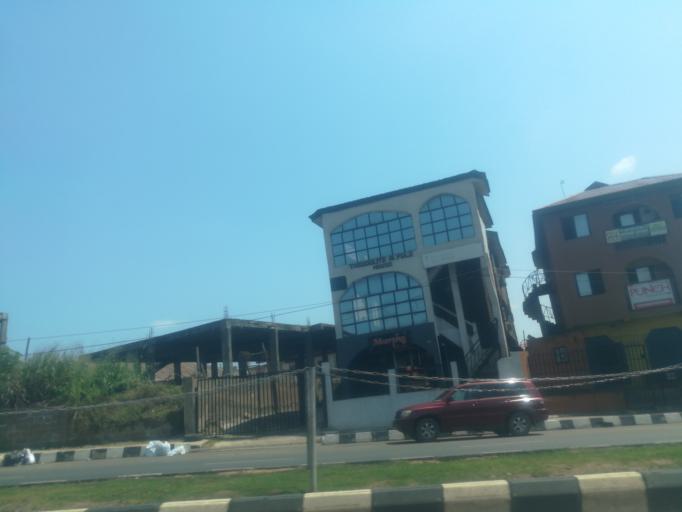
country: NG
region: Ogun
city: Abeokuta
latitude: 7.1560
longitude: 3.3674
